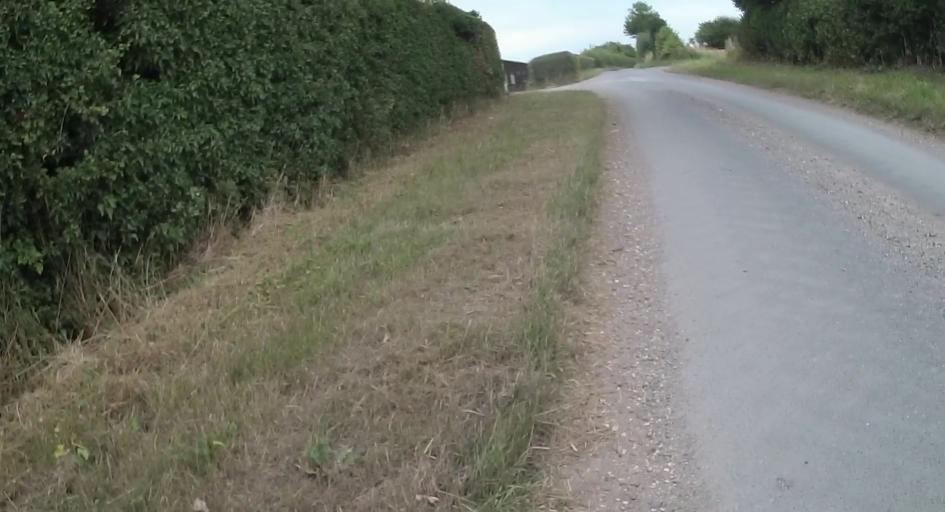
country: GB
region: England
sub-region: Hampshire
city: Kings Worthy
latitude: 51.1647
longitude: -1.2997
